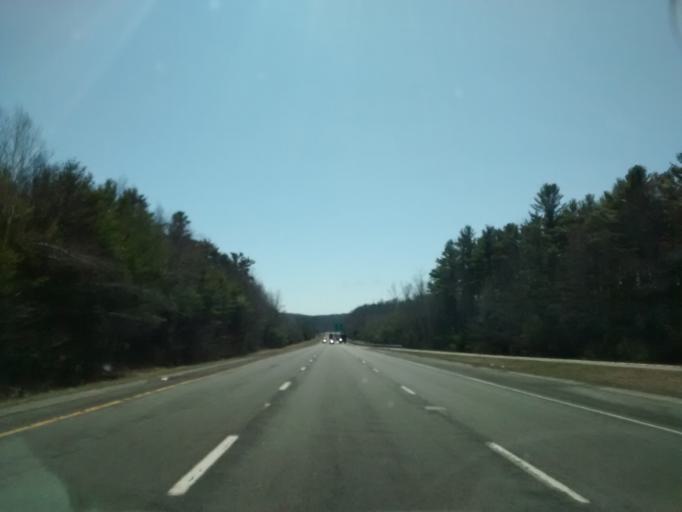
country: US
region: Massachusetts
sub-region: Hampden County
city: Holland
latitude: 42.0363
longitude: -72.1316
